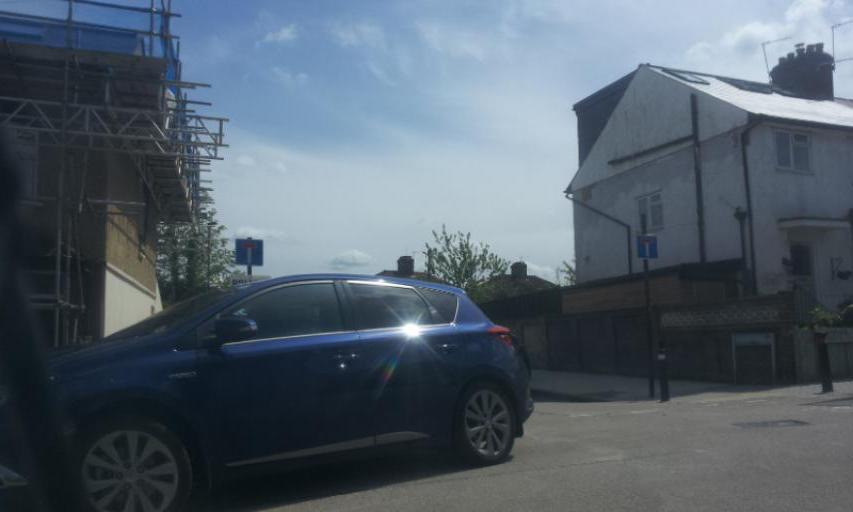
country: GB
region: England
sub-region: Greater London
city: Catford
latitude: 51.4507
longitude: -0.0302
